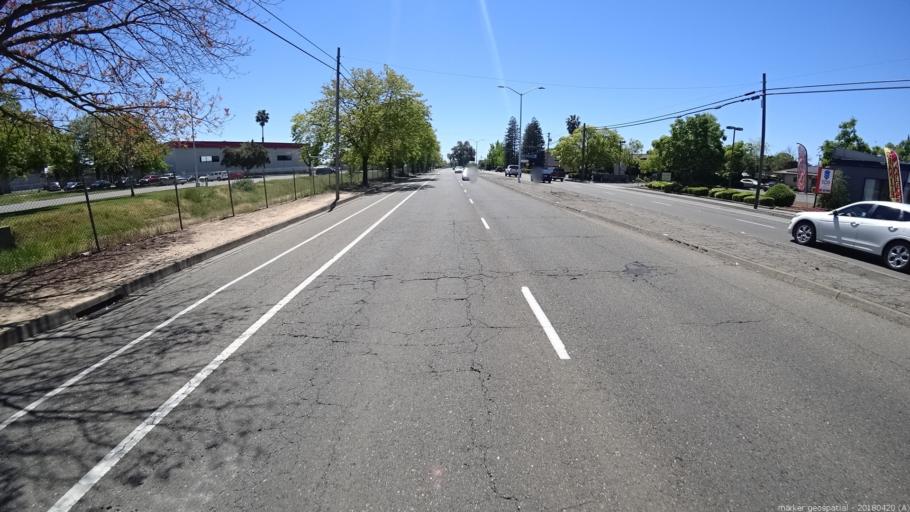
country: US
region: California
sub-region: Sacramento County
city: Parkway
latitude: 38.5165
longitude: -121.4998
